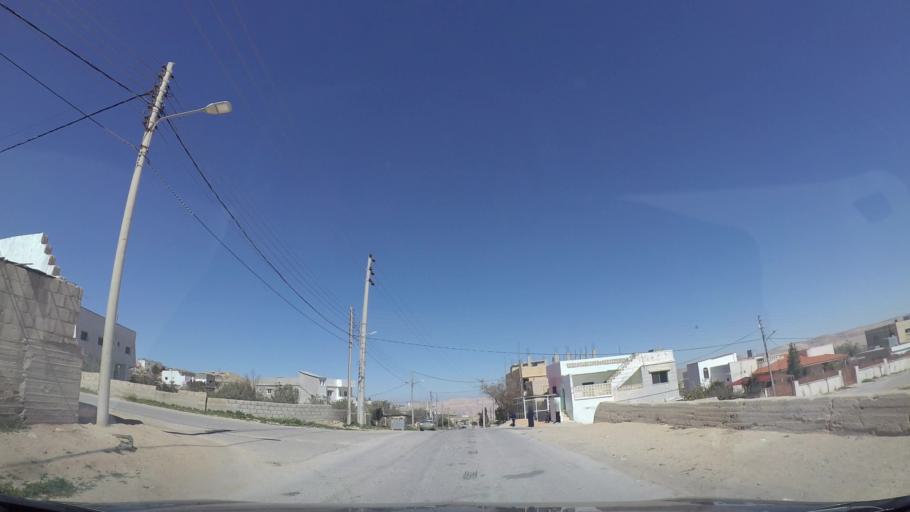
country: JO
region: Tafielah
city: At Tafilah
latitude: 30.8279
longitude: 35.5798
